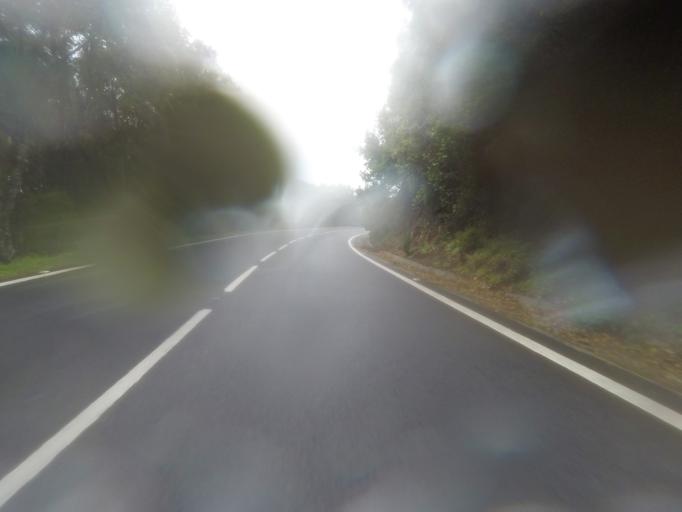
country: ES
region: Canary Islands
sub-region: Provincia de Santa Cruz de Tenerife
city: Vallehermosa
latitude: 28.1378
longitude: -17.2817
